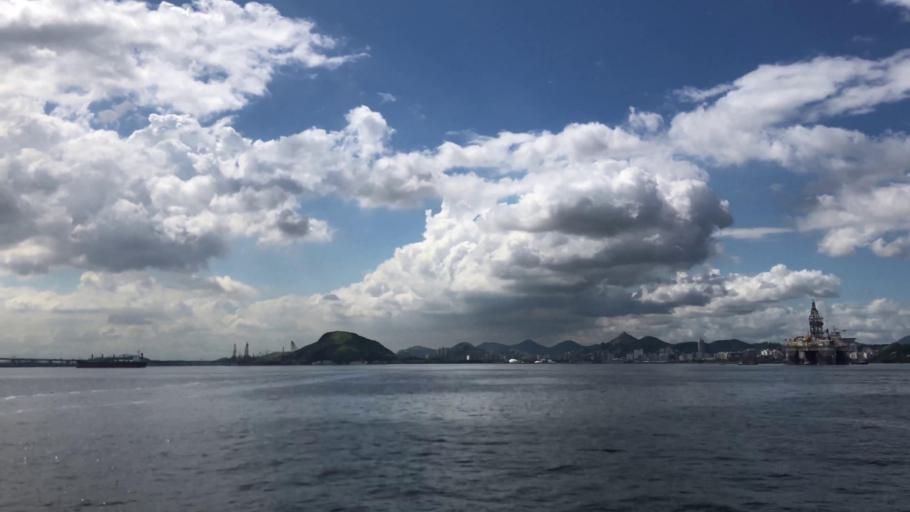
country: BR
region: Rio de Janeiro
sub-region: Rio De Janeiro
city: Rio de Janeiro
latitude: -22.8989
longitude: -43.1560
